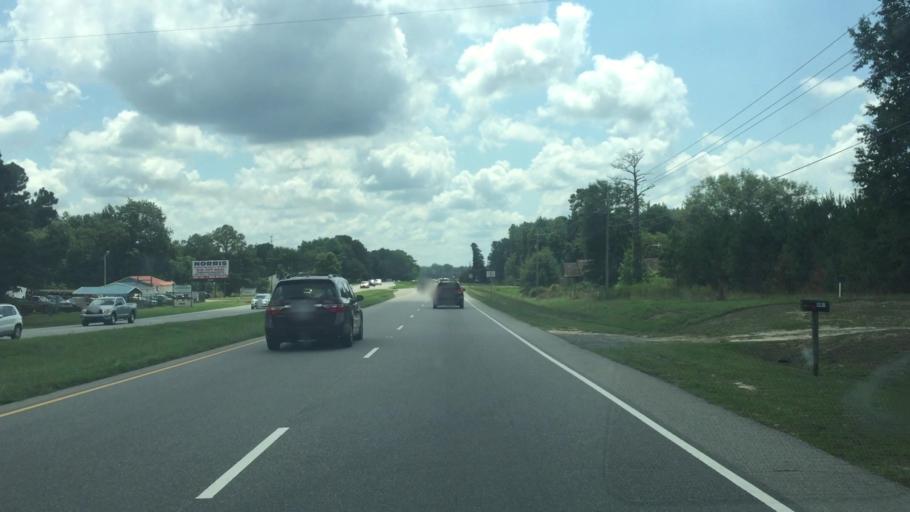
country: US
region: North Carolina
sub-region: Scotland County
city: Laurel Hill
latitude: 34.8234
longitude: -79.5843
